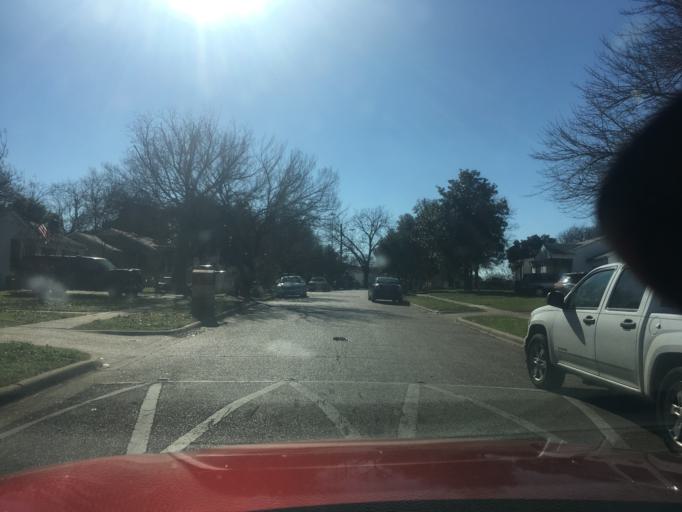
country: US
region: Texas
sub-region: Dallas County
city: Cockrell Hill
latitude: 32.7067
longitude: -96.8324
